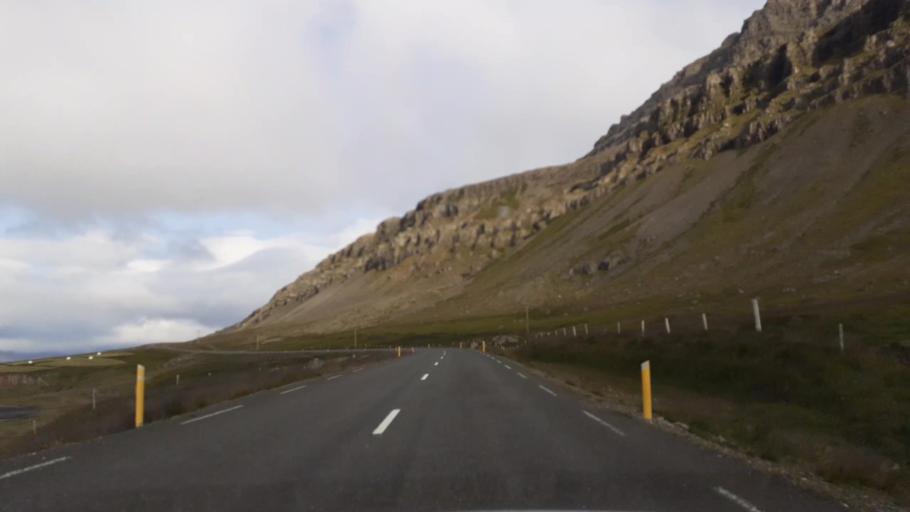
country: IS
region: East
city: Eskifjoerdur
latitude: 64.7973
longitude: -13.9644
